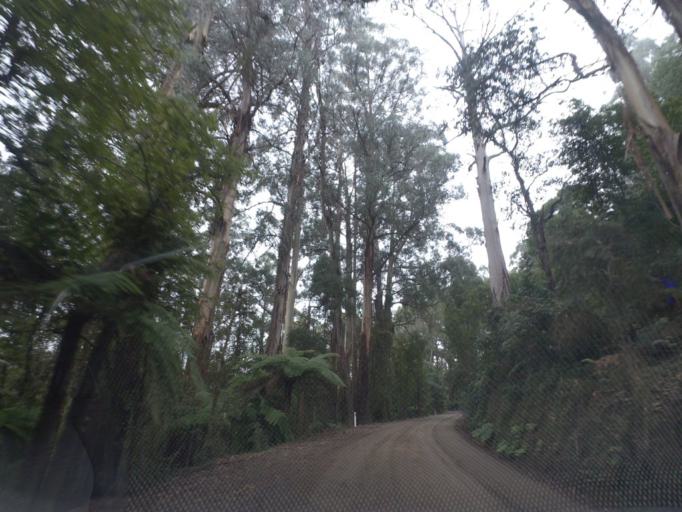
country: AU
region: Victoria
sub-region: Yarra Ranges
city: Launching Place
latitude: -37.7132
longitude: 145.5885
